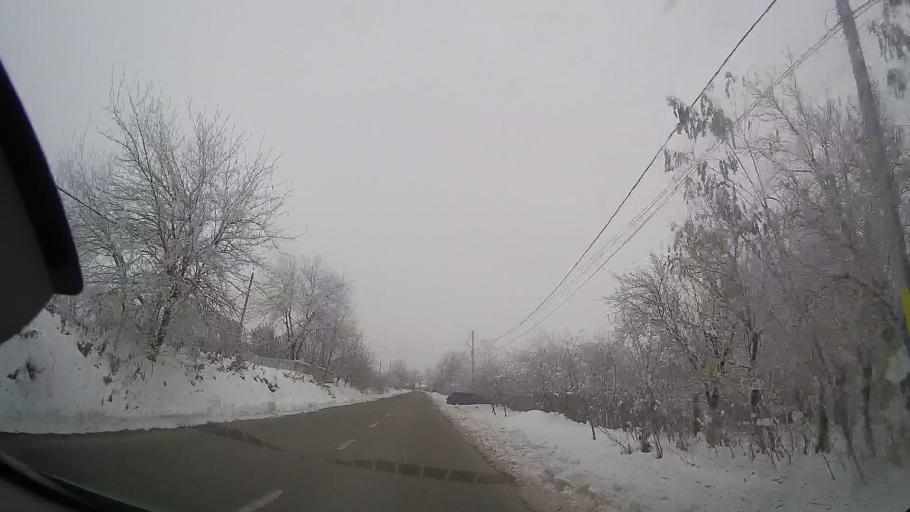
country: RO
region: Neamt
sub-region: Comuna Icusesti
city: Balusesti
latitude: 46.8619
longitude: 27.0057
